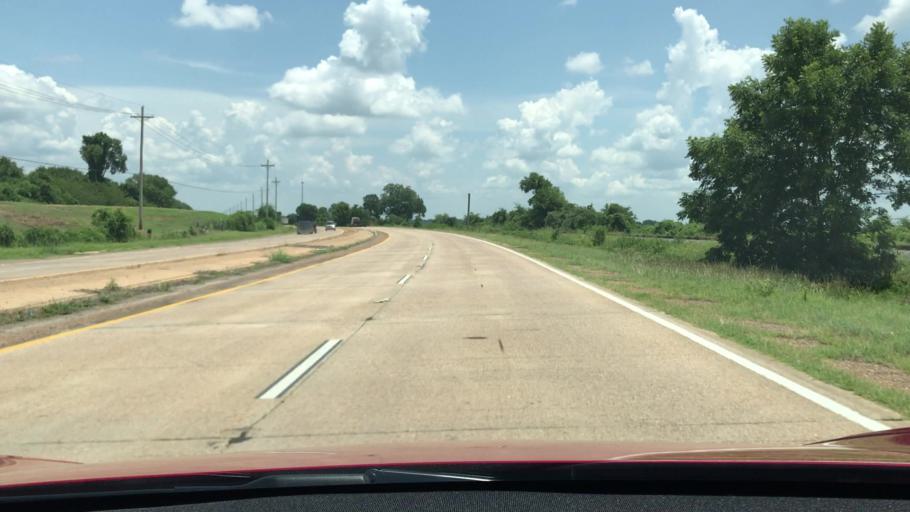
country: US
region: Louisiana
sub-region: Bossier Parish
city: Bossier City
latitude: 32.3895
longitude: -93.6829
